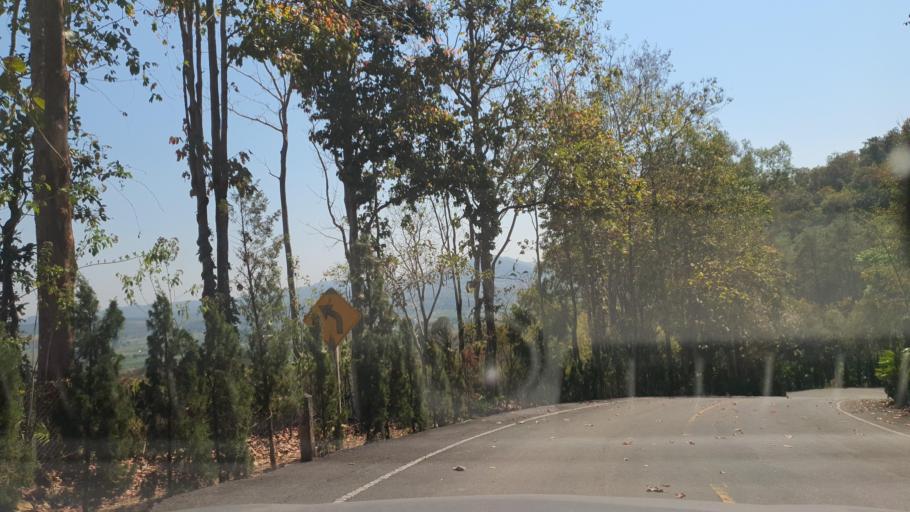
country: TH
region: Lampang
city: Wang Nuea
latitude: 19.1821
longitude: 99.4985
